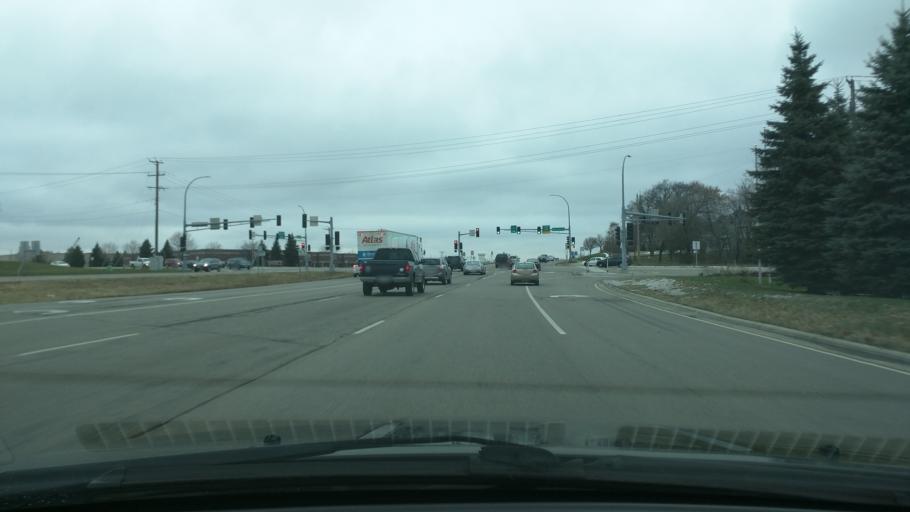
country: US
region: Minnesota
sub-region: Dakota County
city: Mendota Heights
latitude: 44.8471
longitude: -93.1254
